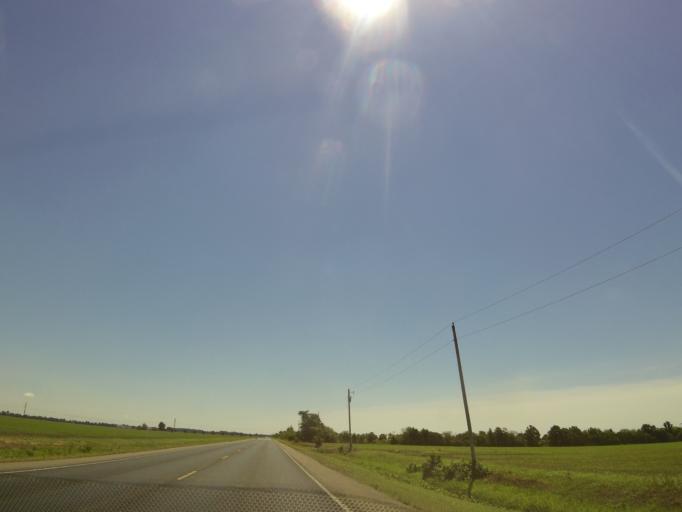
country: US
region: Missouri
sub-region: New Madrid County
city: Lilbourn
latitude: 36.5551
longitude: -89.6540
